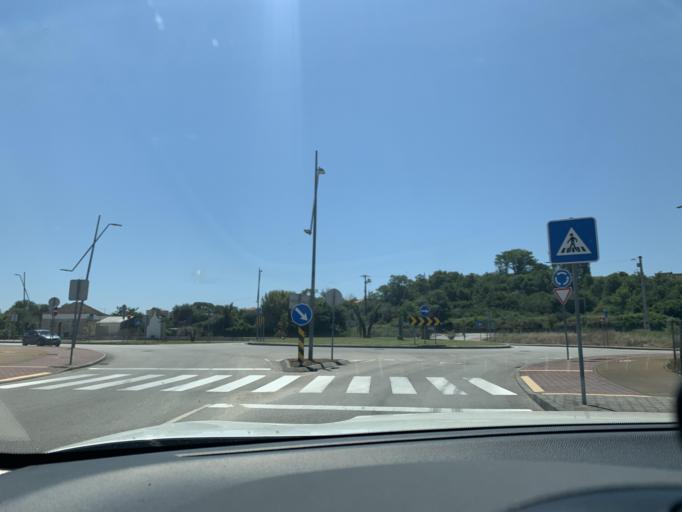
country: PT
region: Viseu
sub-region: Mangualde
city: Mangualde
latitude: 40.6085
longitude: -7.7573
